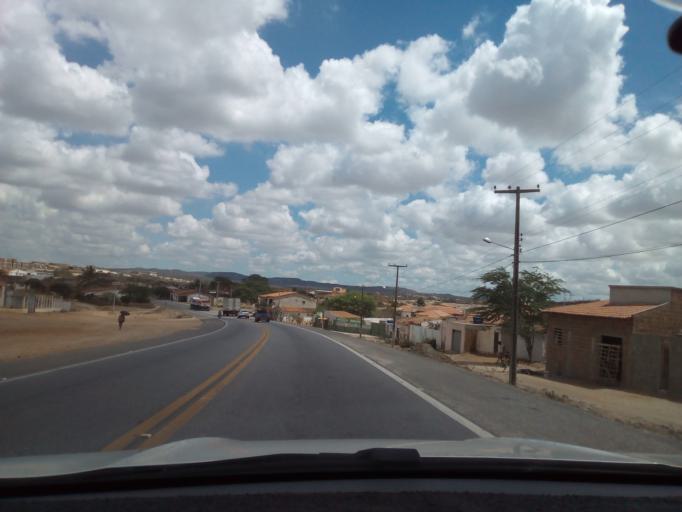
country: BR
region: Paraiba
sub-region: Soledade
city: Soledade
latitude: -7.0595
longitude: -36.3563
